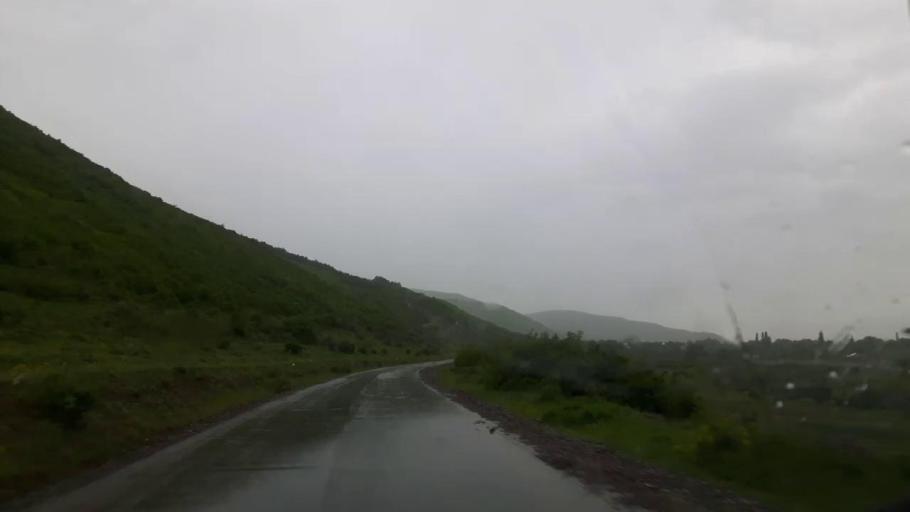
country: GE
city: Agara
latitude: 41.9831
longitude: 43.9292
